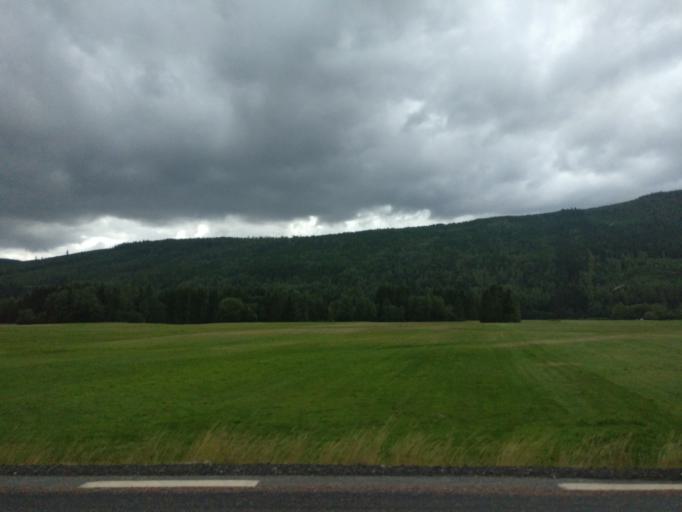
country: SE
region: Vaermland
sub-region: Torsby Kommun
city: Torsby
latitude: 60.7041
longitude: 12.9000
